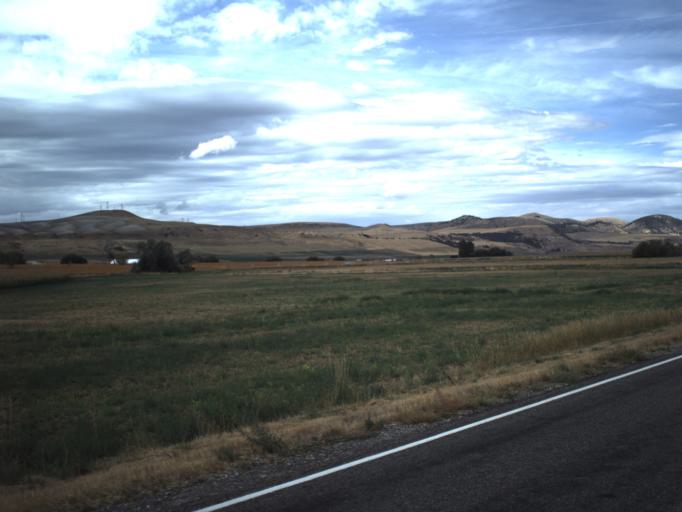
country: US
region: Utah
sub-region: Cache County
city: Lewiston
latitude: 41.9233
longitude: -111.9530
